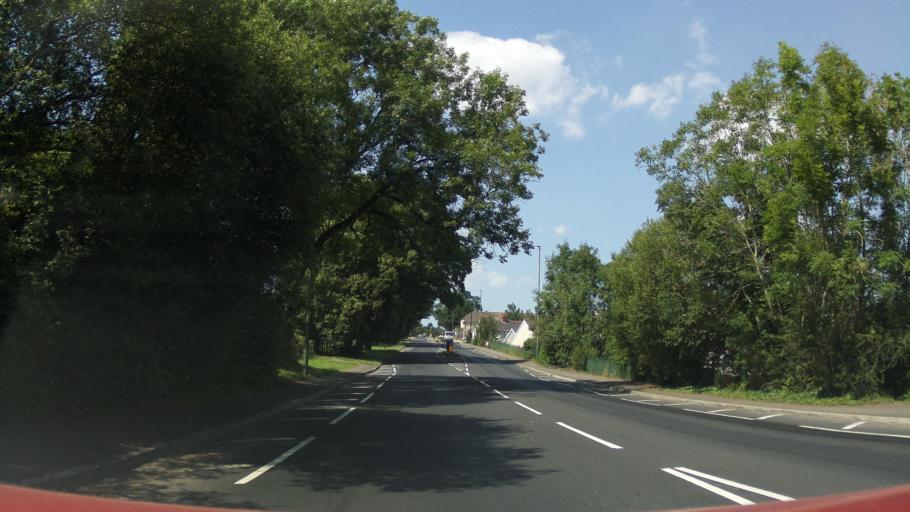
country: GB
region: Wales
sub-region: Caerphilly County Borough
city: Pengam
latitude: 51.6606
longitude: -3.2281
